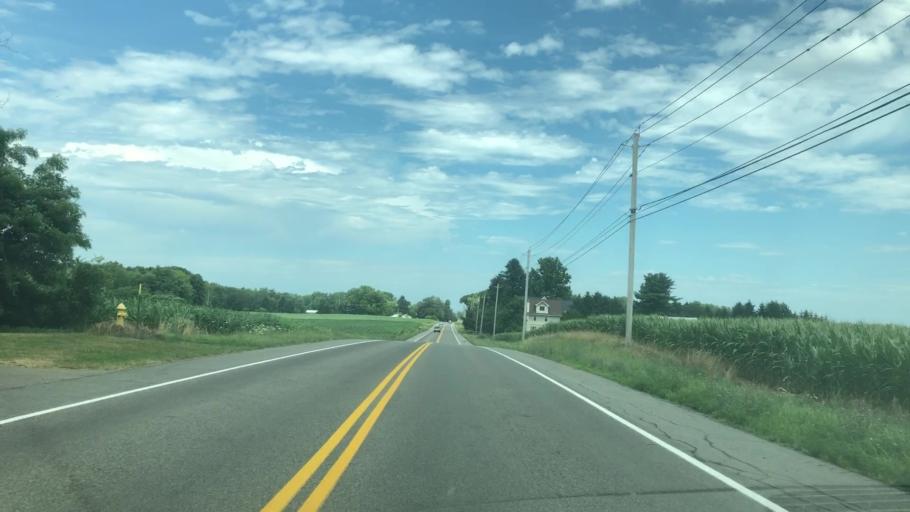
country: US
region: New York
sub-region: Monroe County
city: Webster
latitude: 43.2060
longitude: -77.4004
